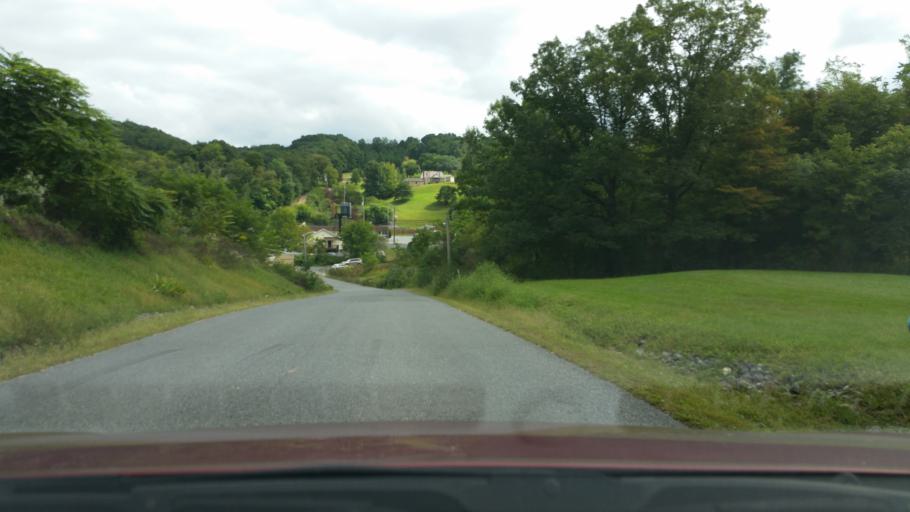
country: US
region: West Virginia
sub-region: Morgan County
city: Berkeley Springs
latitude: 39.6043
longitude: -78.2417
